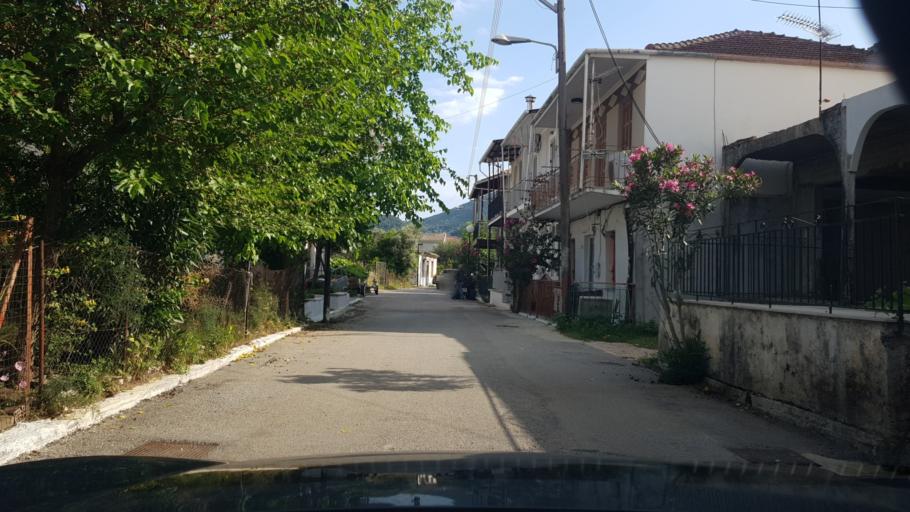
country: GR
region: Ionian Islands
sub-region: Lefkada
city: Nidri
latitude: 38.6818
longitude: 20.6979
